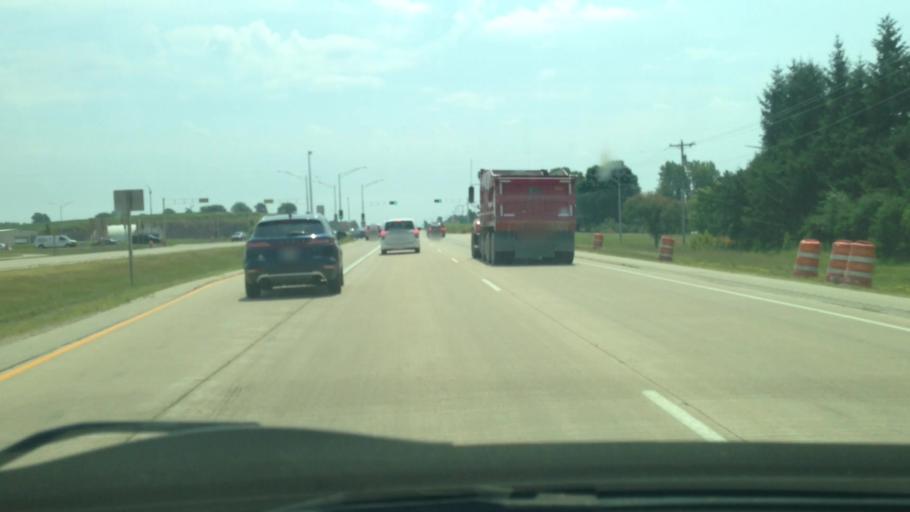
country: US
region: Wisconsin
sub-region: Dane County
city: Waunakee
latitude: 43.1879
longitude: -89.5562
